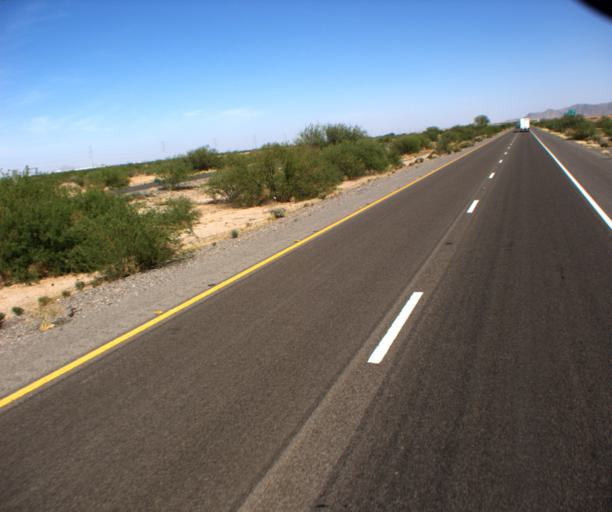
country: US
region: Arizona
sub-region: Pinal County
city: Casa Grande
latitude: 32.8279
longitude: -111.8373
